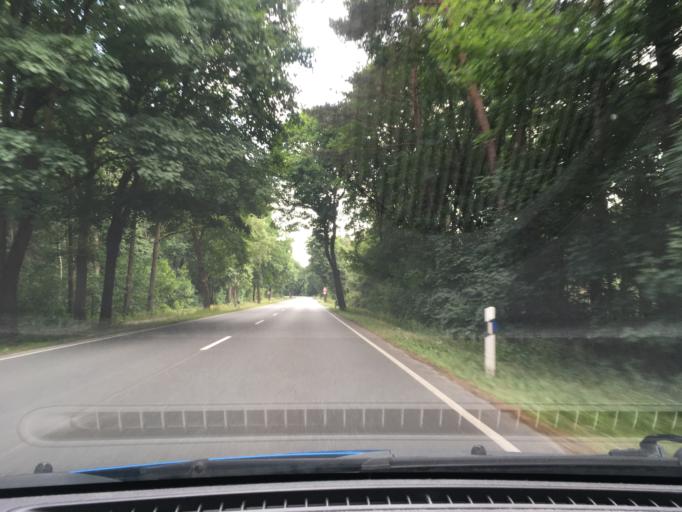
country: DE
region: Lower Saxony
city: Kakenstorf
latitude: 53.2942
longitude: 9.7946
